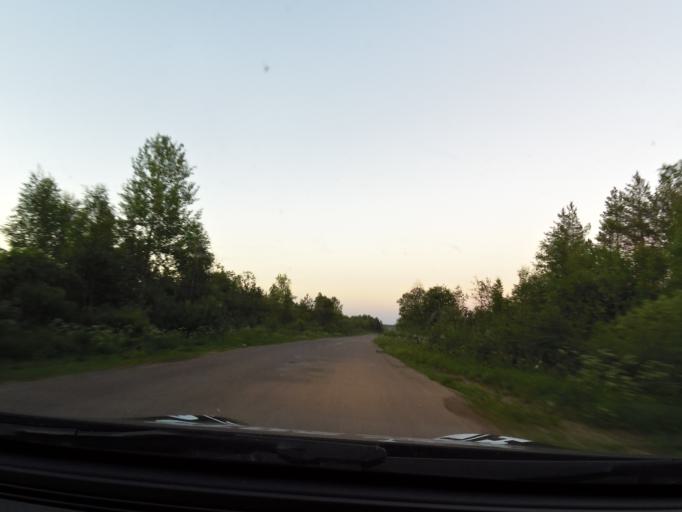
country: RU
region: Vologda
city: Vytegra
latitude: 60.8678
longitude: 35.9791
